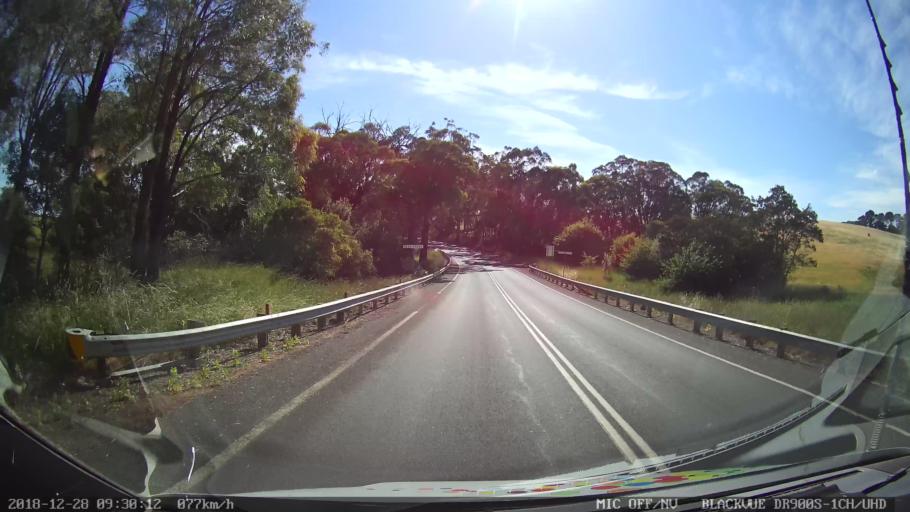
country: AU
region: New South Wales
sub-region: Upper Lachlan Shire
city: Crookwell
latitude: -34.4502
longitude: 149.4370
